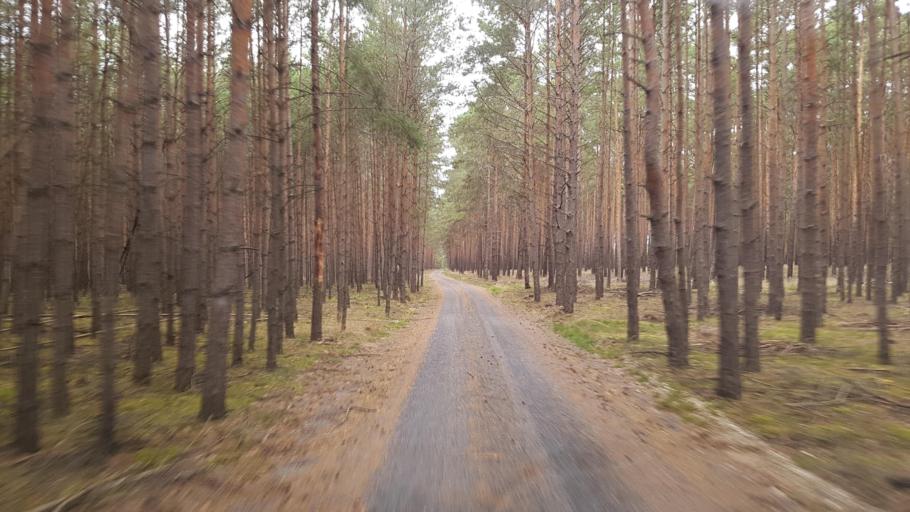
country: DE
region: Brandenburg
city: Sonnewalde
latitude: 51.7263
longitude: 13.6650
